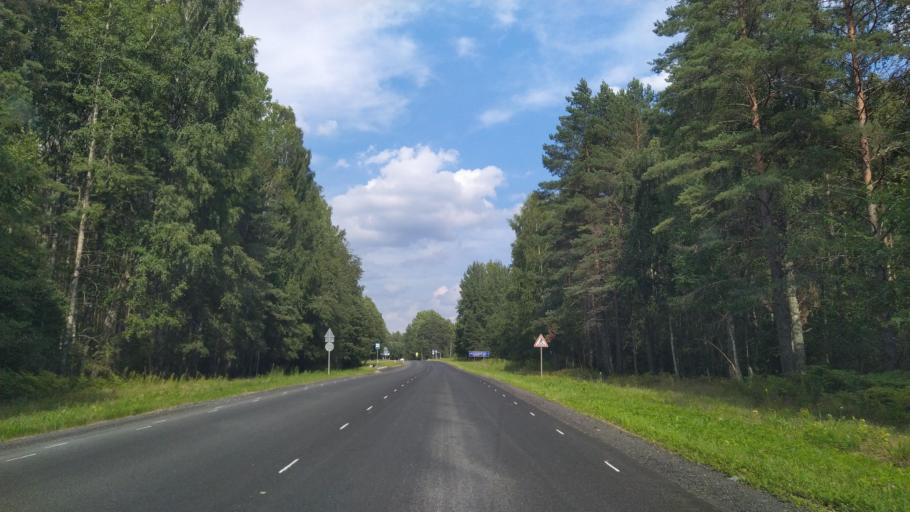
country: RU
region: Pskov
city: Porkhov
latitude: 57.7363
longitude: 29.4144
